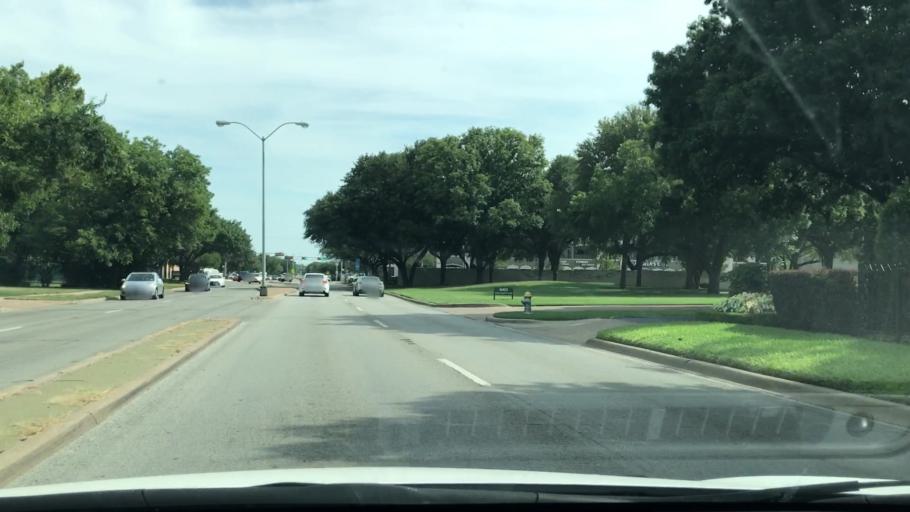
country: US
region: Texas
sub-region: Dallas County
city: University Park
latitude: 32.8531
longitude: -96.8213
